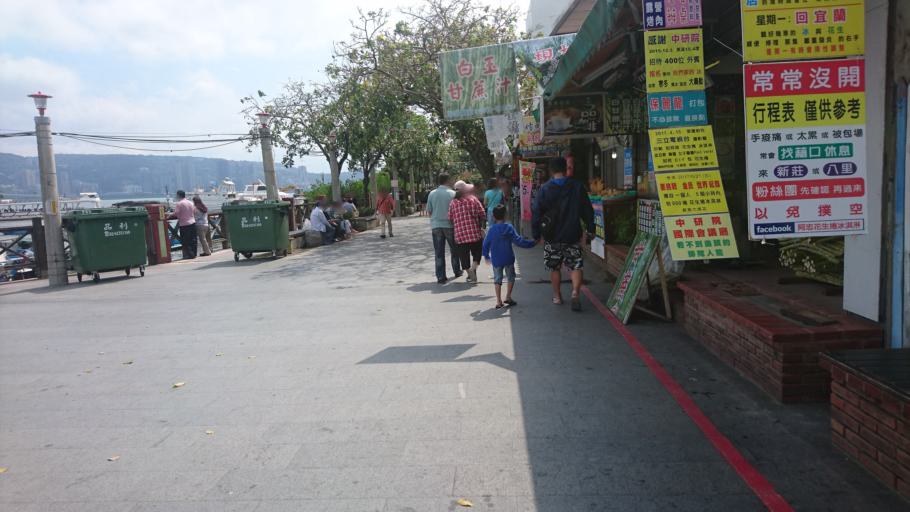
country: TW
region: Taipei
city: Taipei
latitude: 25.1595
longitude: 121.4342
